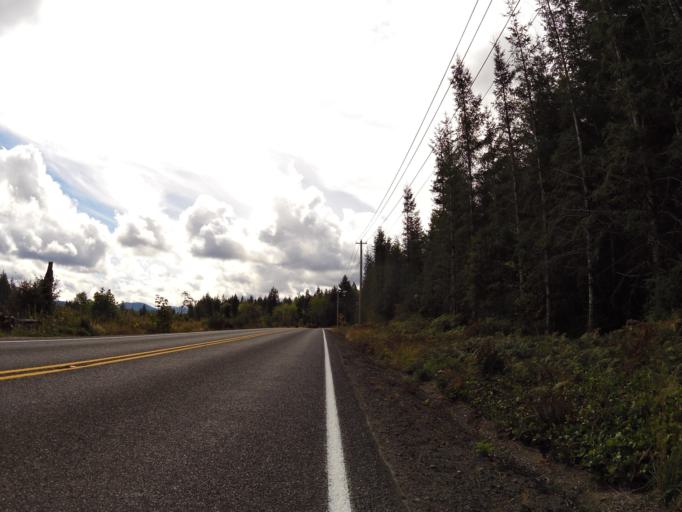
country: US
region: Washington
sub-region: Mason County
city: Shelton
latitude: 47.1447
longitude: -123.0829
